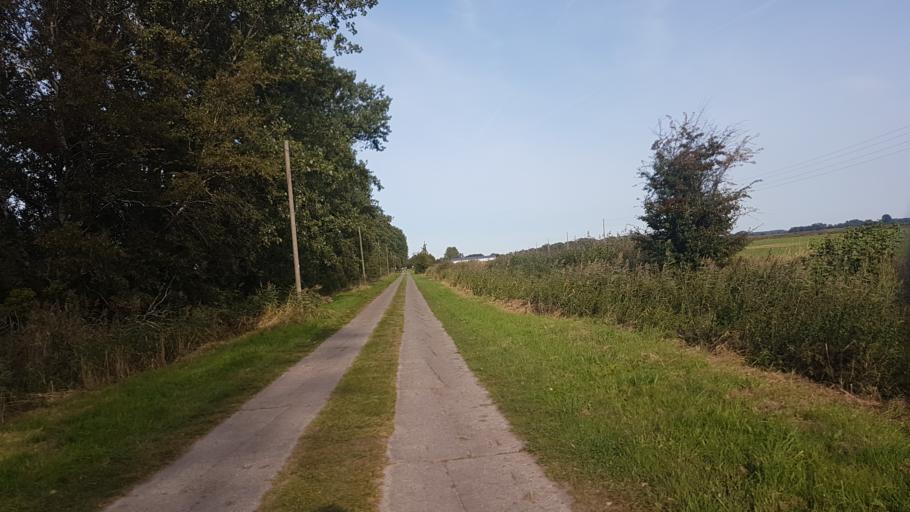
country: DE
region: Mecklenburg-Vorpommern
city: Rambin
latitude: 54.4487
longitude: 13.1364
